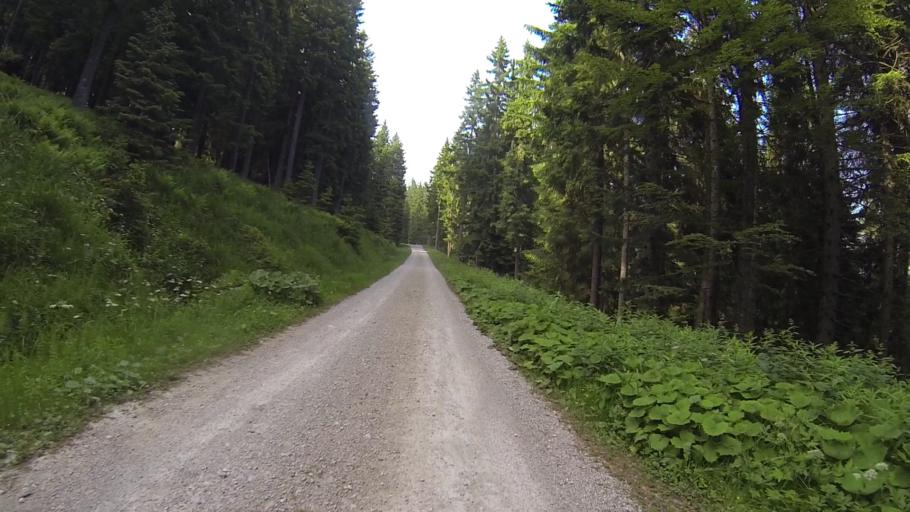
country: DE
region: Bavaria
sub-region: Swabia
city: Nesselwang
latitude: 47.5901
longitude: 10.5076
